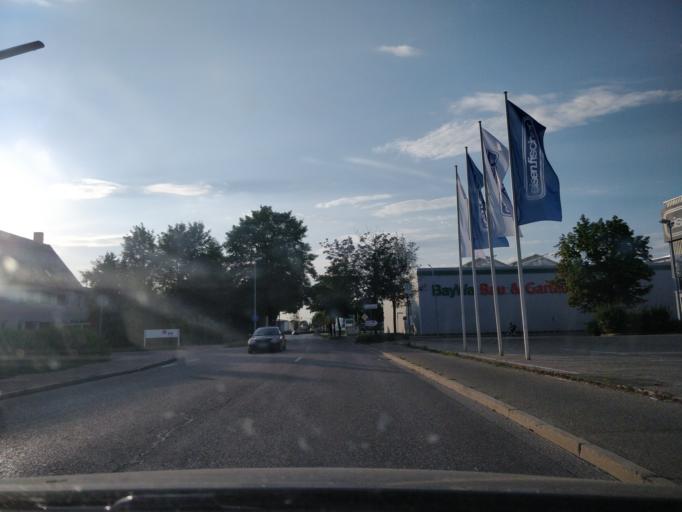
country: DE
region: Bavaria
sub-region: Swabia
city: Noerdlingen
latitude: 48.8594
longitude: 10.5047
